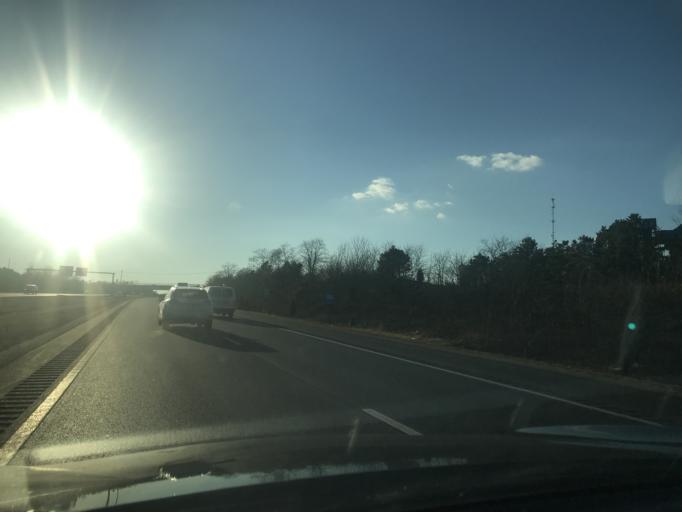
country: US
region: Massachusetts
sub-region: Plymouth County
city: North Plymouth
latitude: 41.9617
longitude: -70.7050
